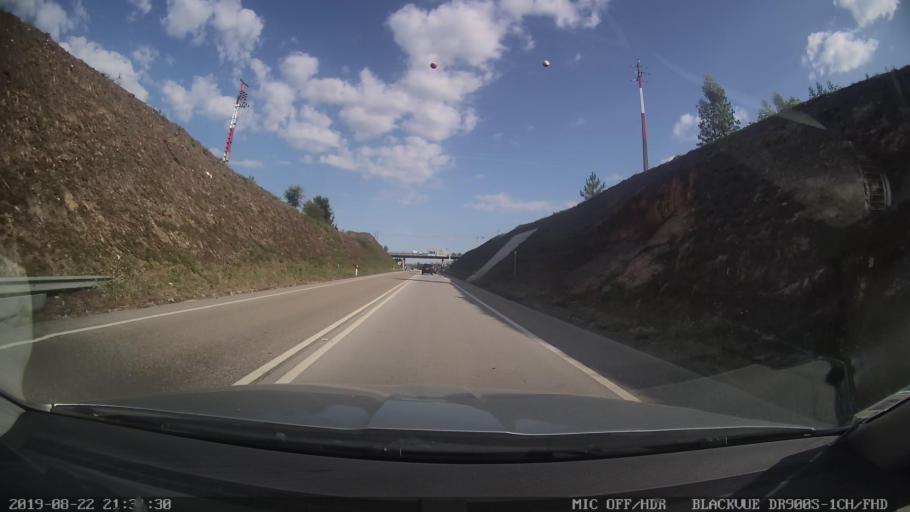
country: PT
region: Leiria
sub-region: Pedrogao Grande
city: Pedrogao Grande
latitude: 39.9208
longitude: -8.1548
